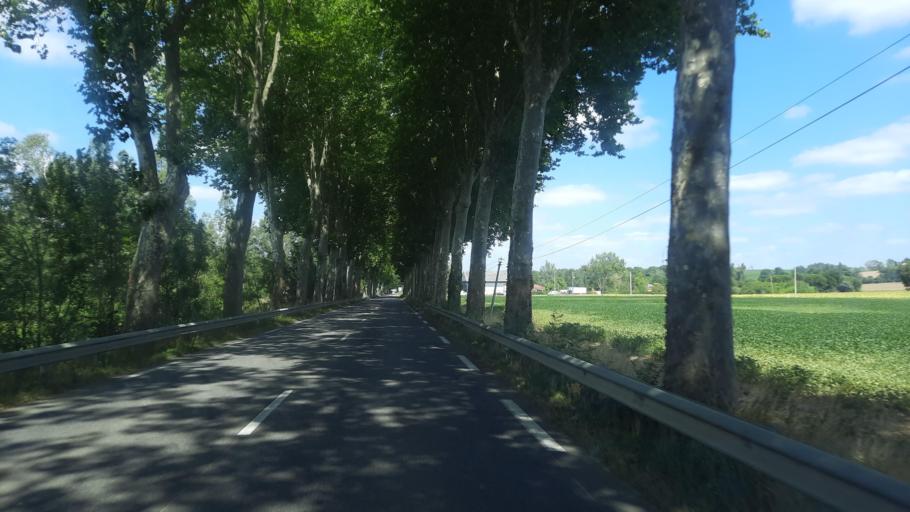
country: FR
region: Midi-Pyrenees
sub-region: Departement du Gers
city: Samatan
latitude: 43.4810
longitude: 0.9267
